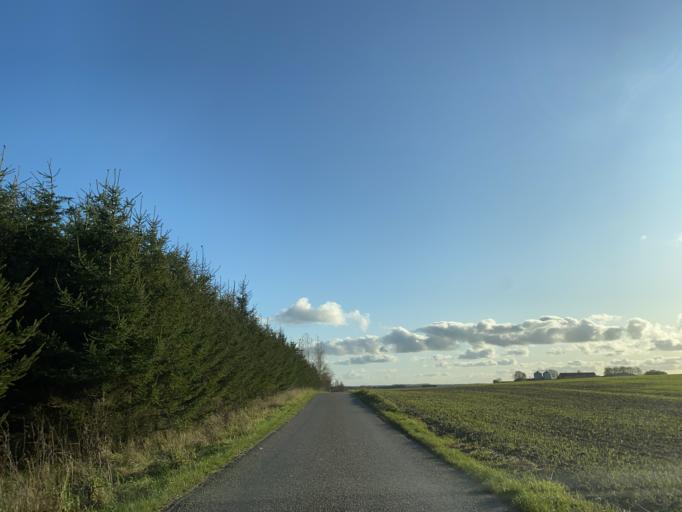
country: DK
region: Central Jutland
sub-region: Viborg Kommune
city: Bjerringbro
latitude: 56.3396
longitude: 9.7147
